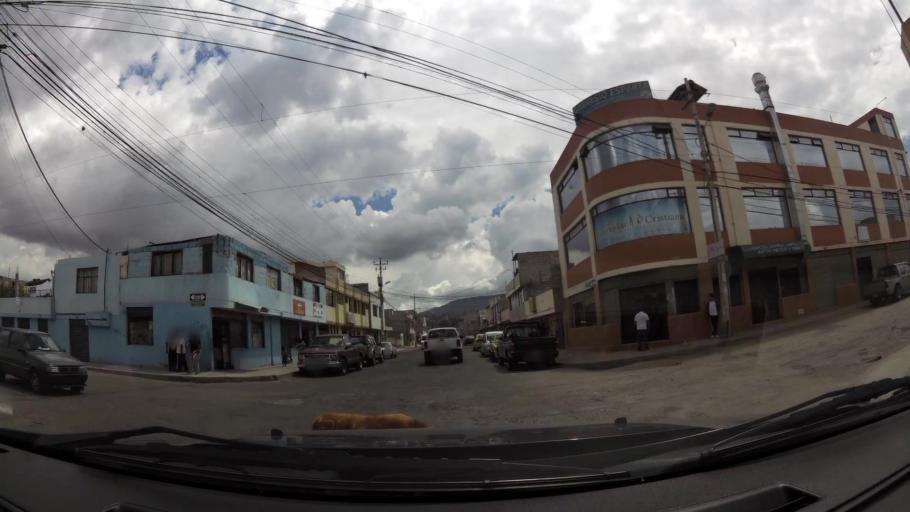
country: EC
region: Pichincha
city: Quito
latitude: -0.0800
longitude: -78.4137
